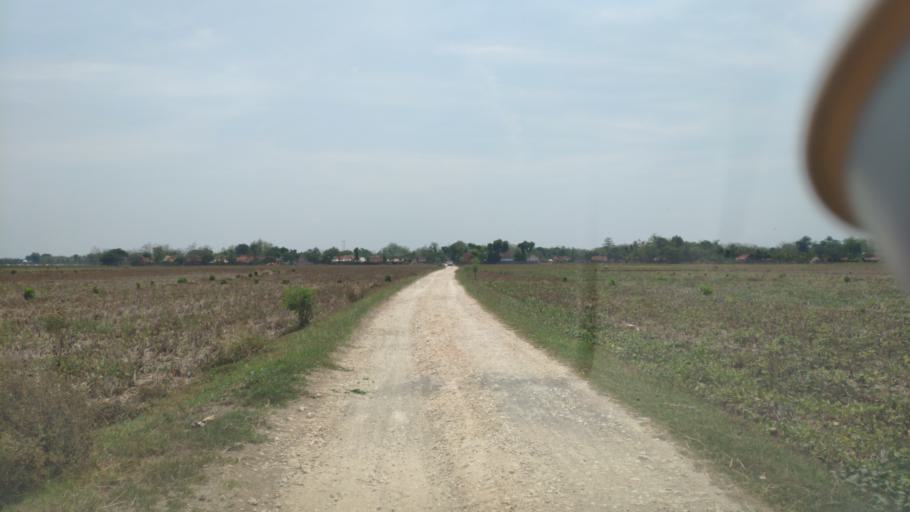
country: ID
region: Central Java
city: Pipes
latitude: -7.0692
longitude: 111.2724
